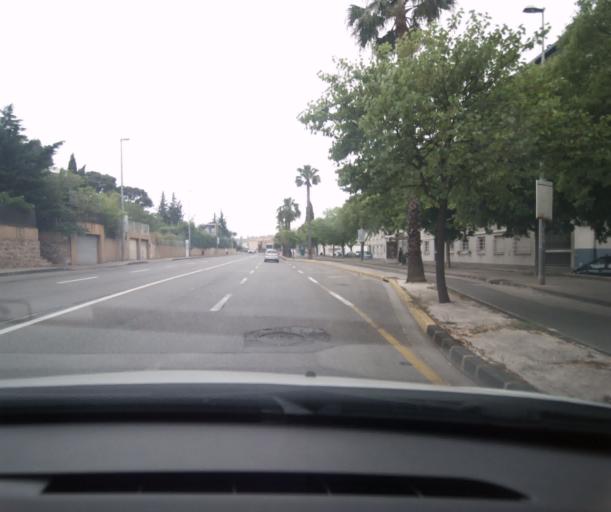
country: FR
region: Provence-Alpes-Cote d'Azur
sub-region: Departement du Var
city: La Valette-du-Var
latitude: 43.1215
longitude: 5.9811
